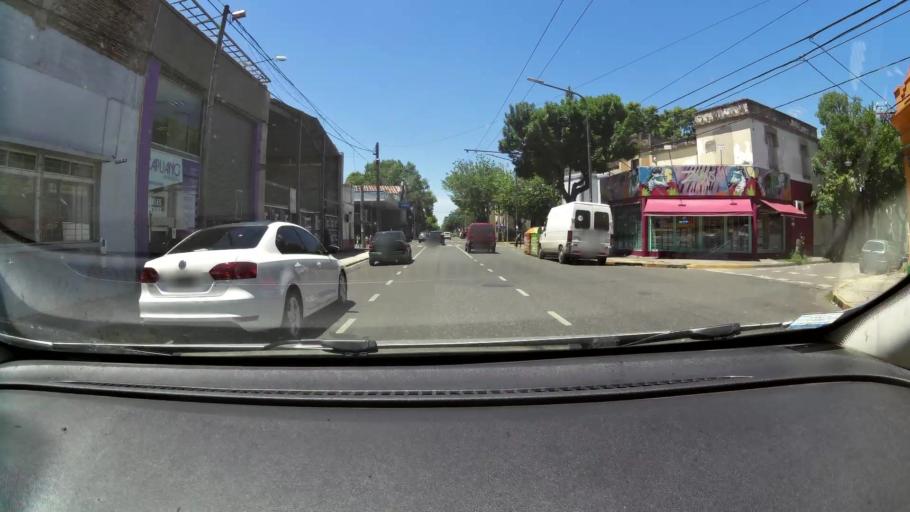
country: AR
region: Santa Fe
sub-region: Departamento de Rosario
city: Rosario
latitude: -32.9418
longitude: -60.6942
